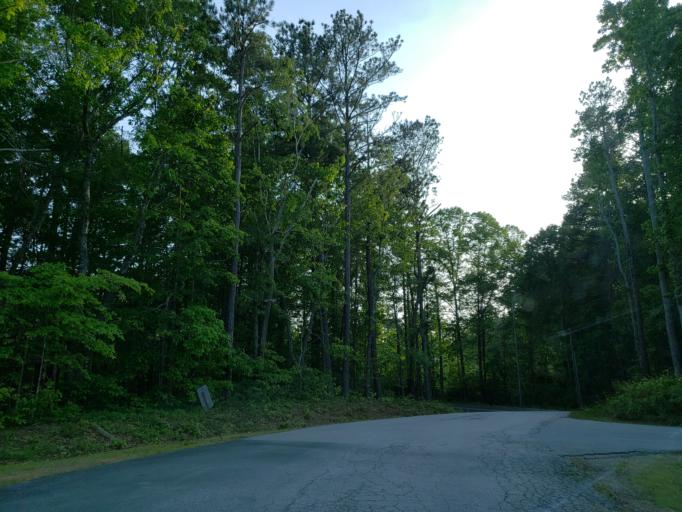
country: US
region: Georgia
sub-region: Carroll County
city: Mount Zion
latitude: 33.6369
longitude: -85.1847
